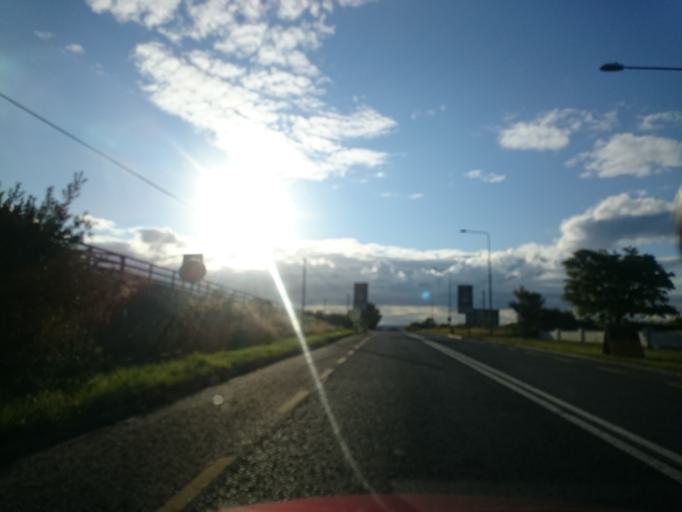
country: IE
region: Leinster
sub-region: Loch Garman
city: Rosslare
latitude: 52.2443
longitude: -6.3925
